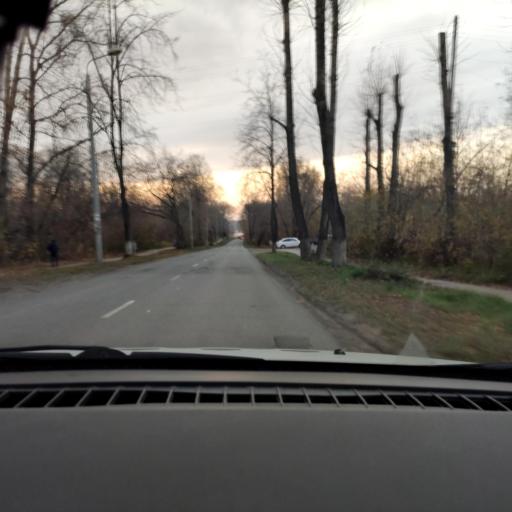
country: RU
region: Perm
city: Perm
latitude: 58.1208
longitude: 56.3774
